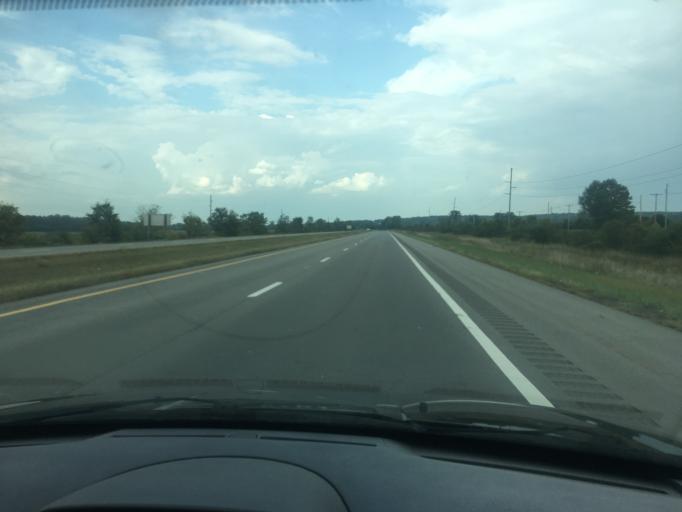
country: US
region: Ohio
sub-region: Clark County
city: Springfield
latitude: 39.9595
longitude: -83.8254
